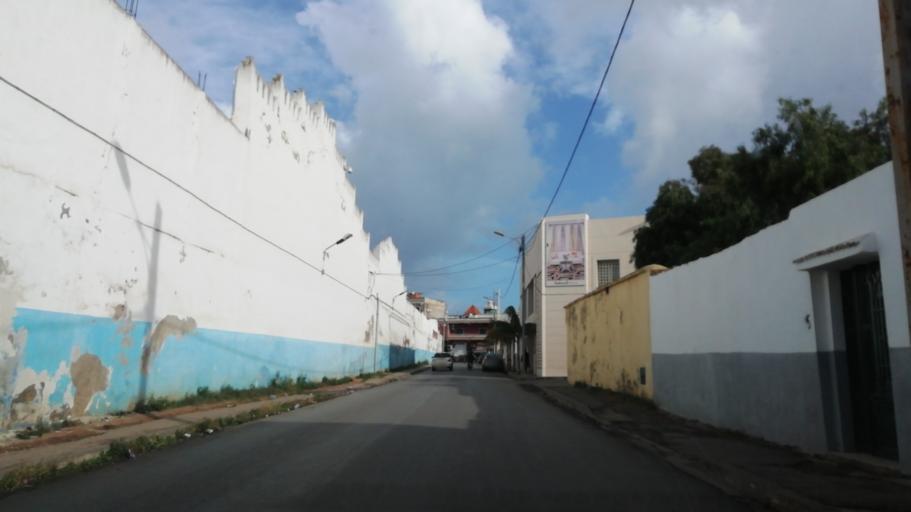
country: DZ
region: Oran
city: Oran
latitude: 35.6918
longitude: -0.6308
